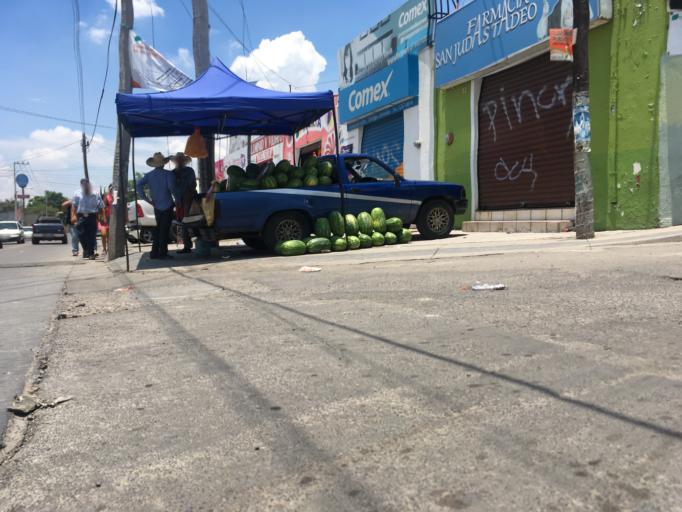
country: MX
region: Jalisco
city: Santa Cruz del Valle
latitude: 20.5316
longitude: -103.4247
